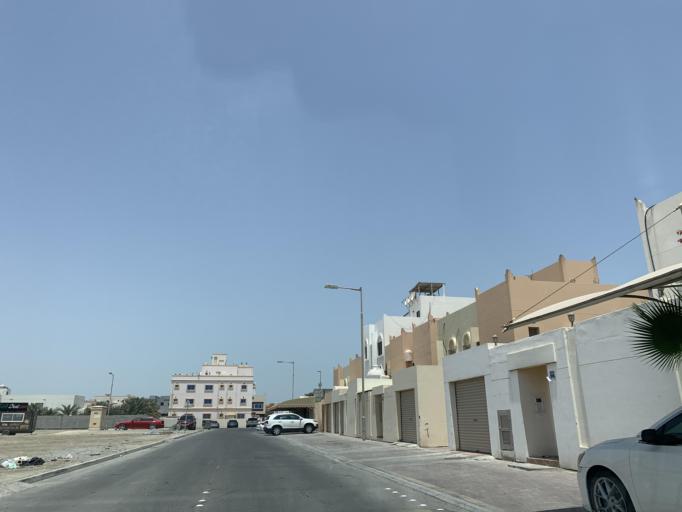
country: BH
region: Northern
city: Sitrah
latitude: 26.1412
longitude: 50.5905
